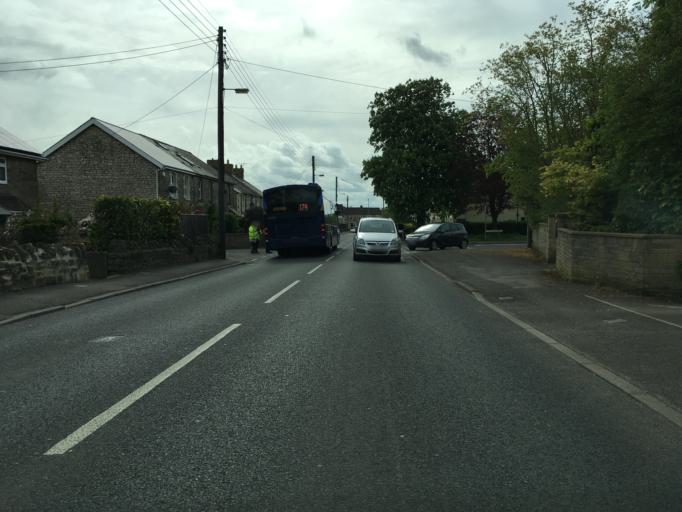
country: GB
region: England
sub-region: Bath and North East Somerset
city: Midsomer Norton
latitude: 51.2792
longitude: -2.4757
